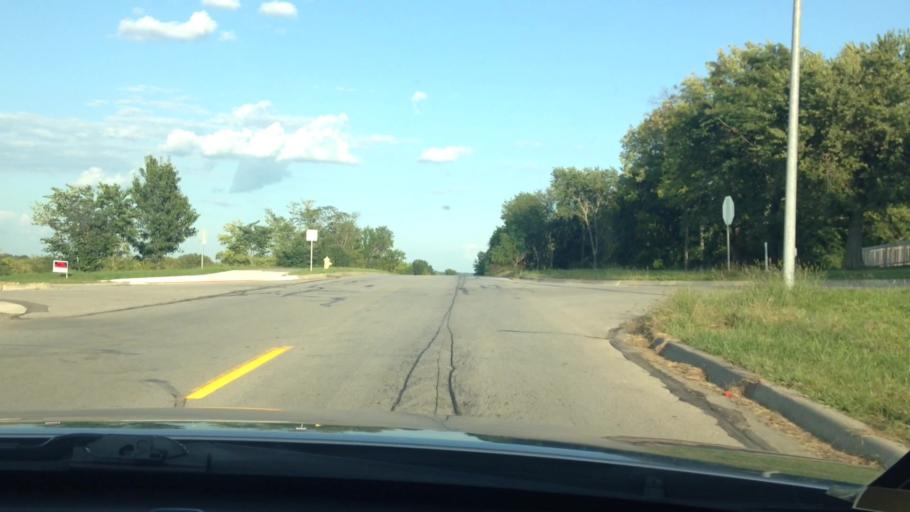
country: US
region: Missouri
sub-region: Jackson County
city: Grandview
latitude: 38.9011
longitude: -94.5148
